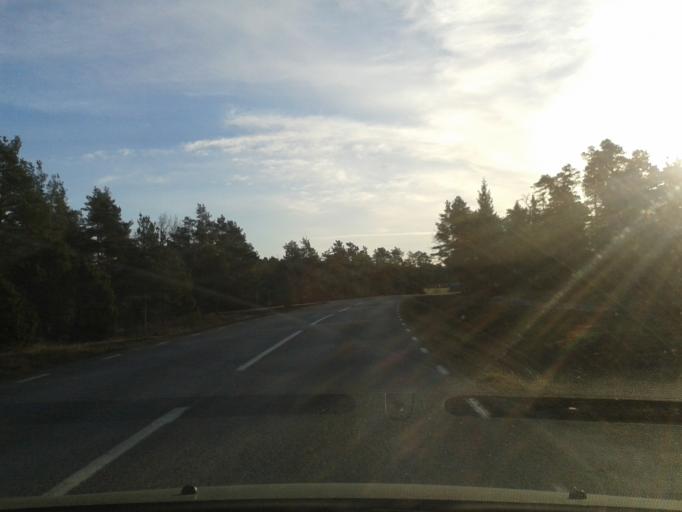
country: SE
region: Gotland
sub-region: Gotland
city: Hemse
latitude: 57.3467
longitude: 18.6922
